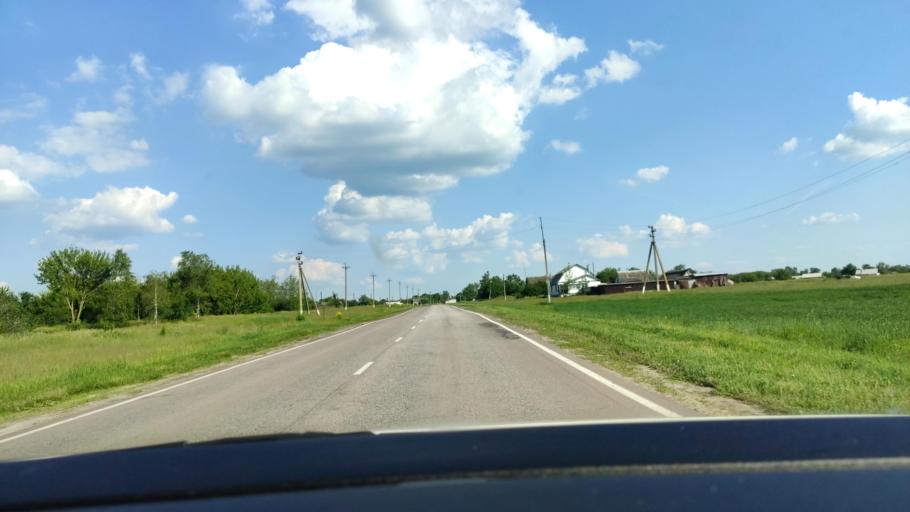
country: RU
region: Voronezj
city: Verkhnyaya Khava
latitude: 51.6845
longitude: 39.9363
